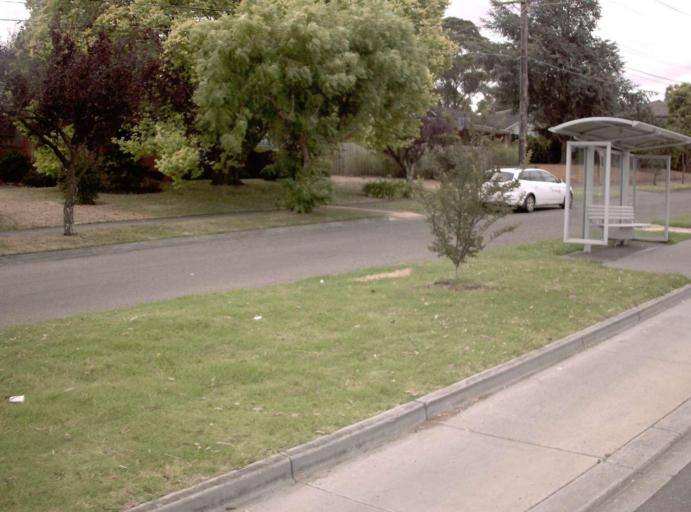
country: AU
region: Victoria
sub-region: Greater Dandenong
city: Dandenong North
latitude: -37.9553
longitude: 145.2262
